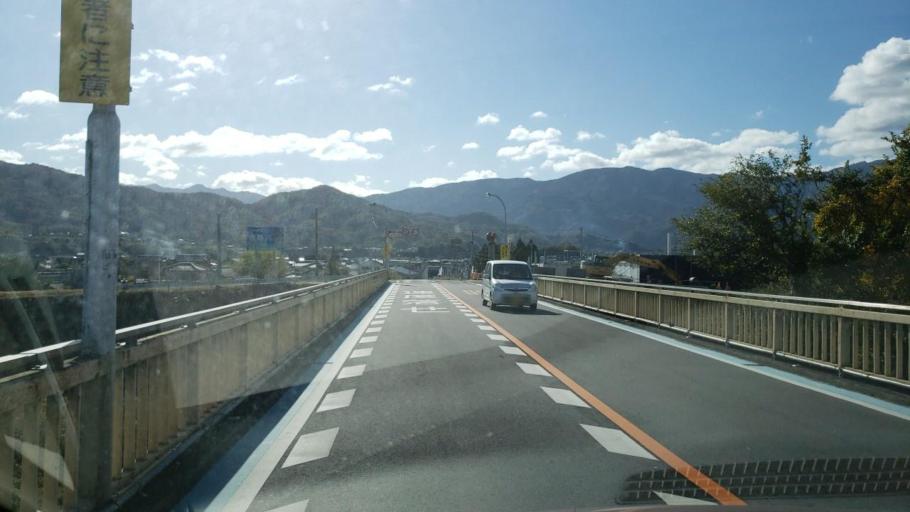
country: JP
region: Tokushima
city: Wakimachi
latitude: 34.0672
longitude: 134.2377
